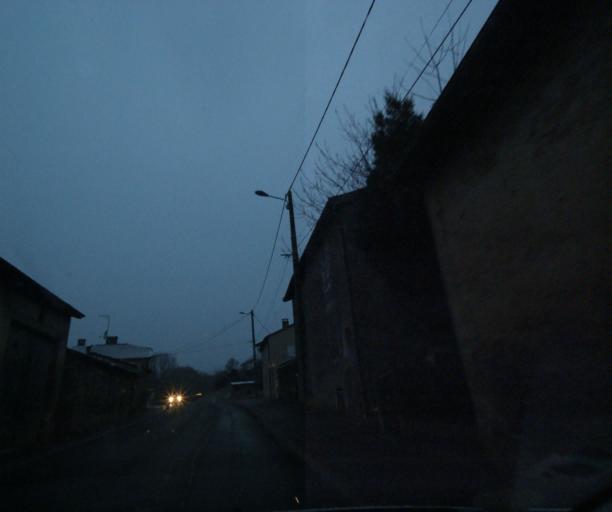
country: FR
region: Champagne-Ardenne
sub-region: Departement de la Haute-Marne
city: Wassy
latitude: 48.4401
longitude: 4.9576
